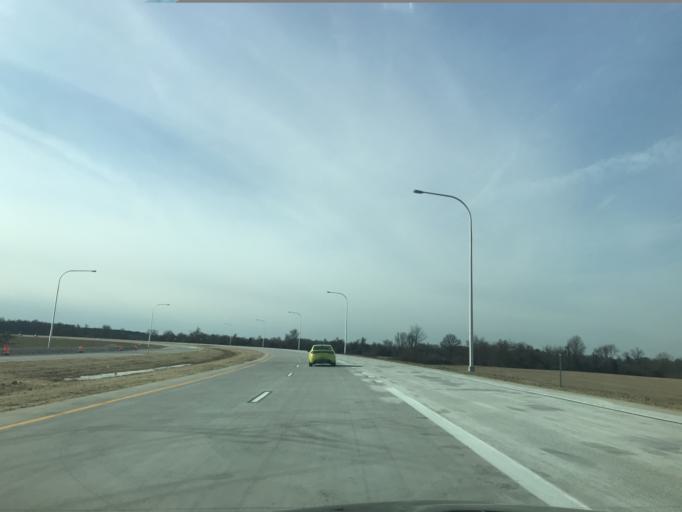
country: US
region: Delaware
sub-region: New Castle County
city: Middletown
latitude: 39.5234
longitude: -75.6857
